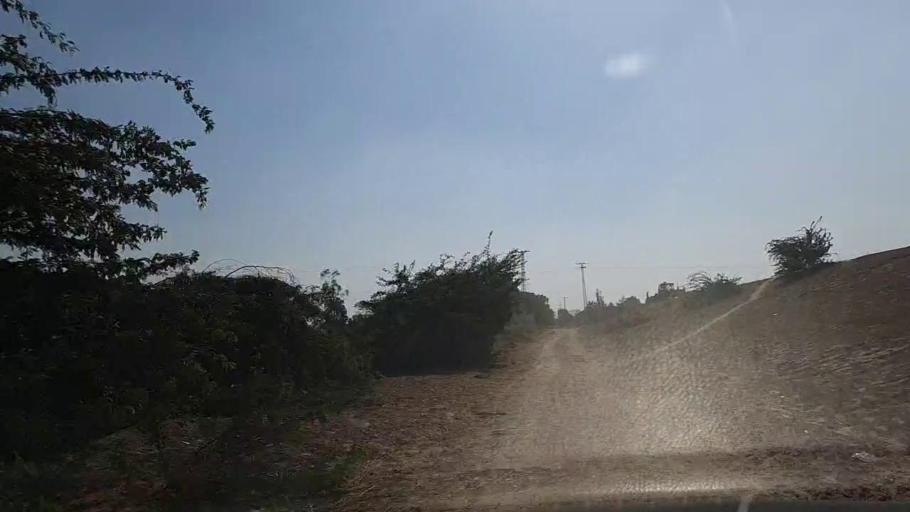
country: PK
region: Sindh
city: Daro Mehar
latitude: 24.7835
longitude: 68.0723
